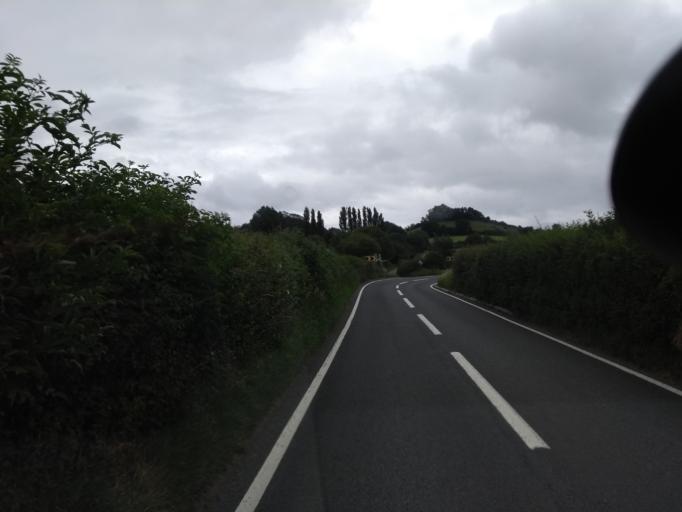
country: GB
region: England
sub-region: Somerset
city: Stoke-sub-Hamdon
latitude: 50.9319
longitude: -2.7648
